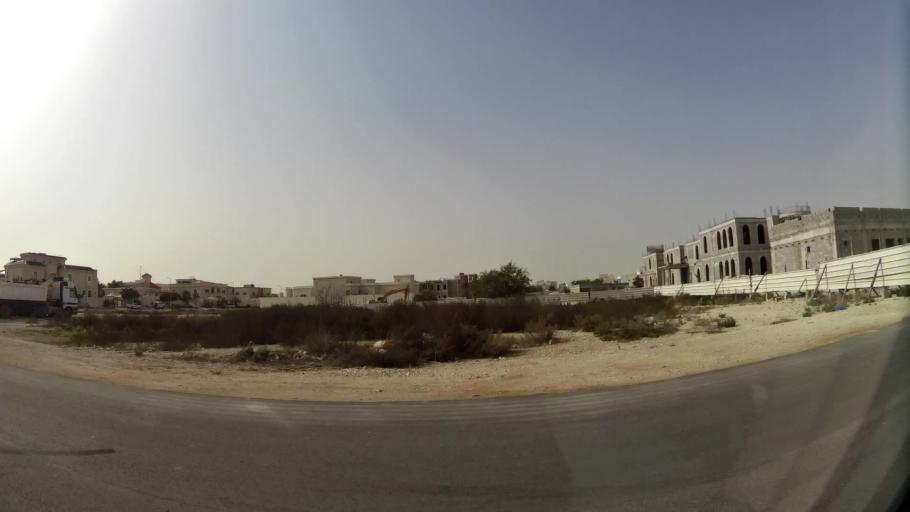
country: QA
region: Baladiyat ar Rayyan
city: Ar Rayyan
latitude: 25.2425
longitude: 51.4411
